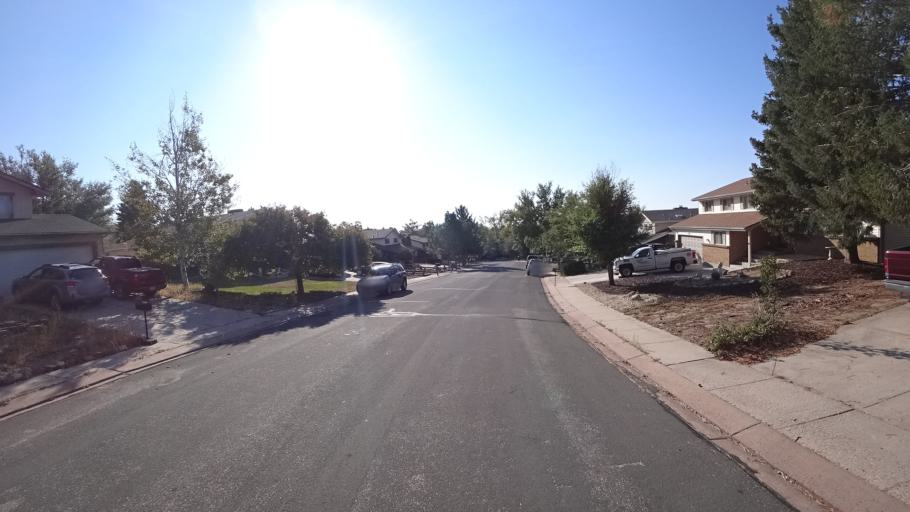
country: US
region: Colorado
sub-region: El Paso County
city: Cimarron Hills
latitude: 38.8861
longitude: -104.7315
